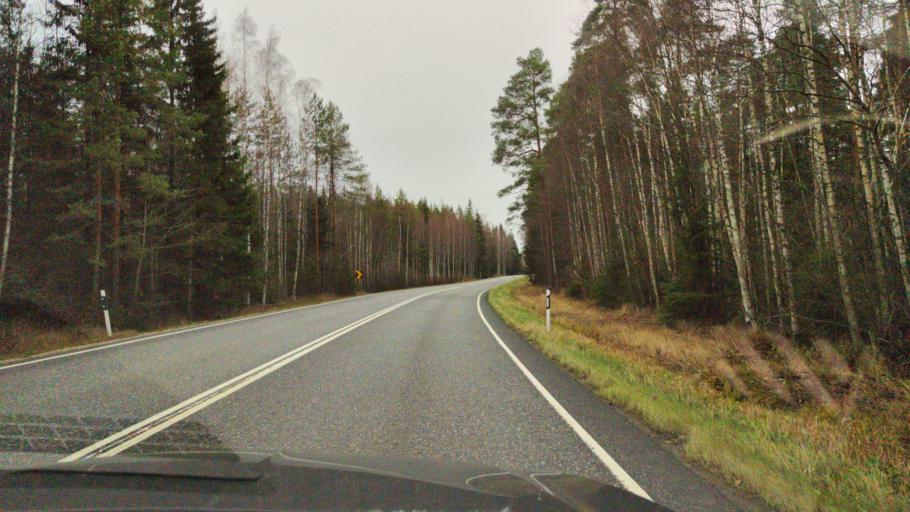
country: FI
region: Varsinais-Suomi
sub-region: Loimaa
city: Ylaene
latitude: 60.7405
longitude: 22.4260
